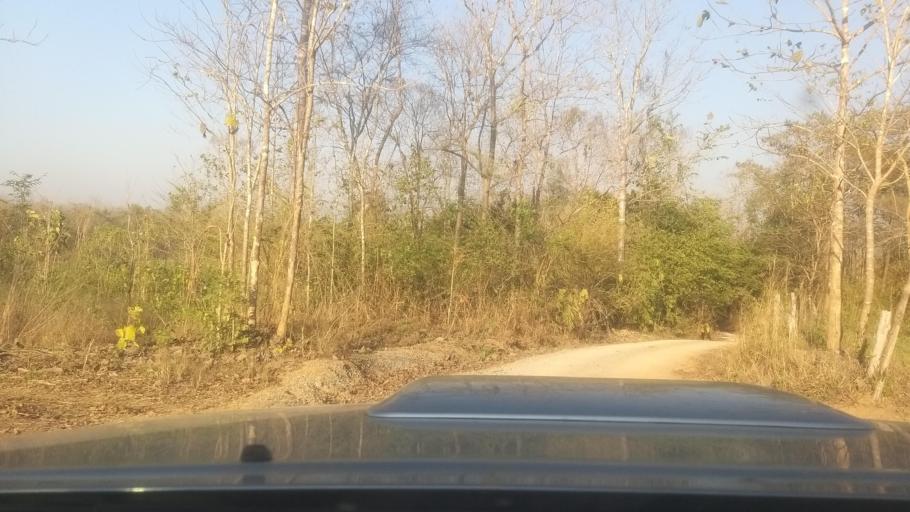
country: TH
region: Phrae
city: Nong Muang Khai
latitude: 18.2665
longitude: 100.0204
